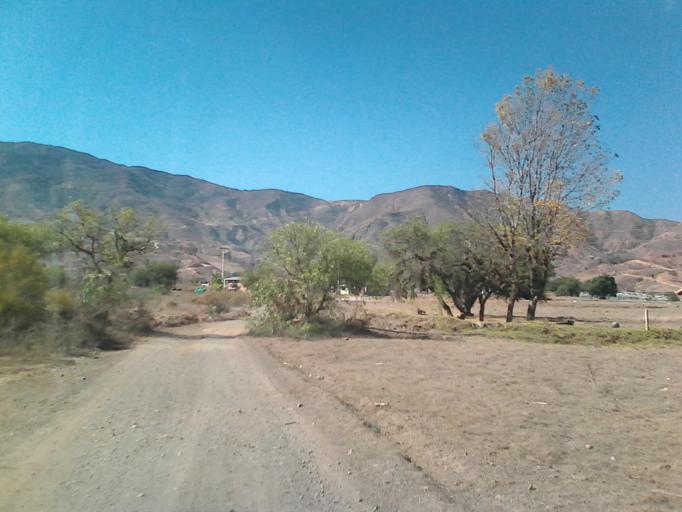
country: CO
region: Boyaca
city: Sachica
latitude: 5.5710
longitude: -73.5440
